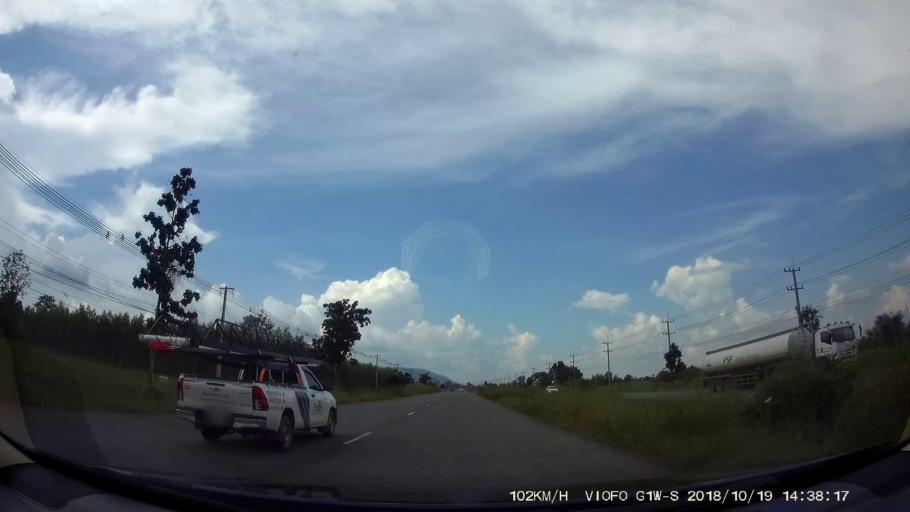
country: TH
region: Chaiyaphum
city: Kaeng Khro
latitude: 16.2108
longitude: 102.2028
